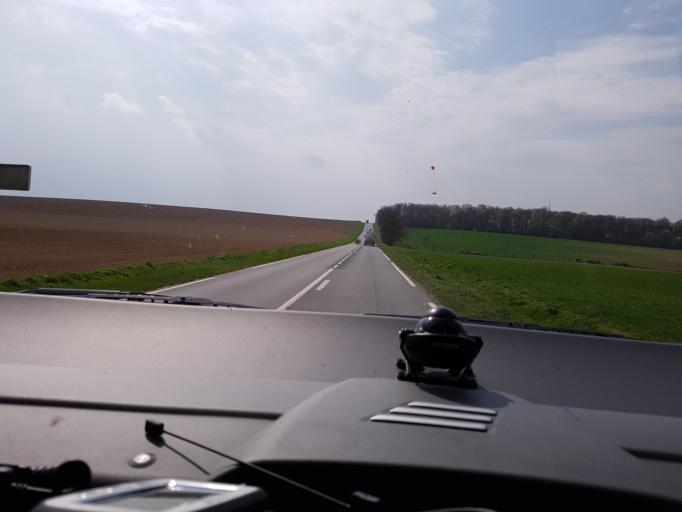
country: FR
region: Picardie
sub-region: Departement de l'Aisne
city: Crouy
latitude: 49.4432
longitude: 3.3581
